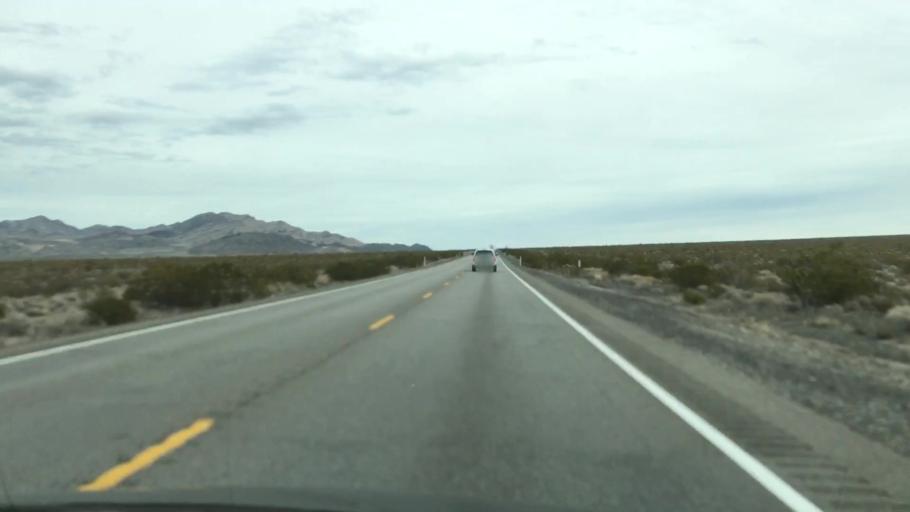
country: US
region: Nevada
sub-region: Nye County
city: Pahrump
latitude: 36.5915
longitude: -116.0340
